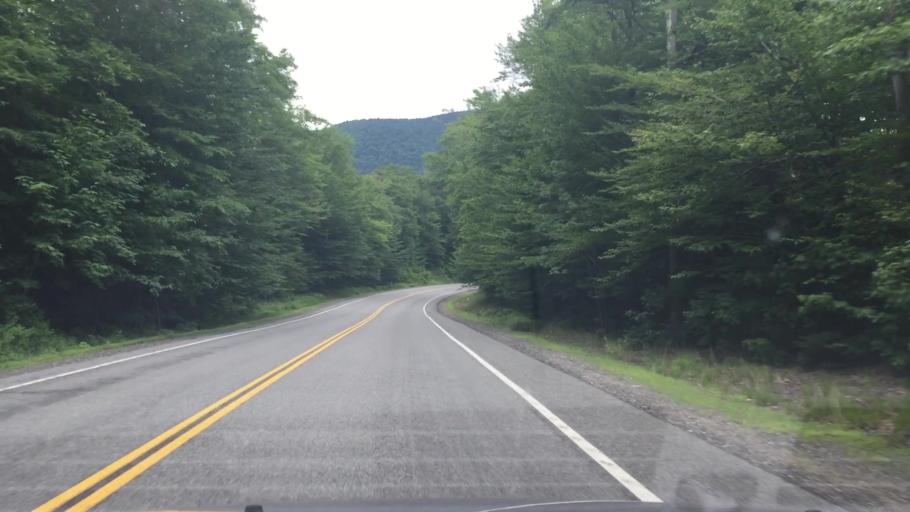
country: US
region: New Hampshire
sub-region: Carroll County
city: North Conway
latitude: 44.0768
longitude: -71.3393
